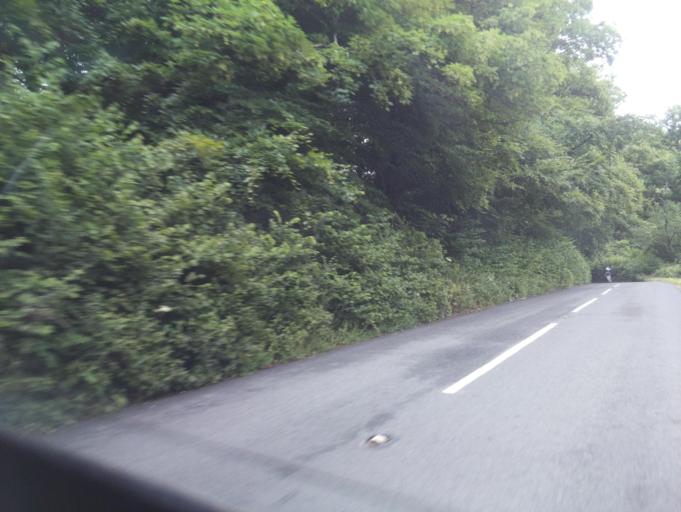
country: GB
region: England
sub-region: Devon
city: Chudleigh
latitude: 50.6238
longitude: -3.6381
